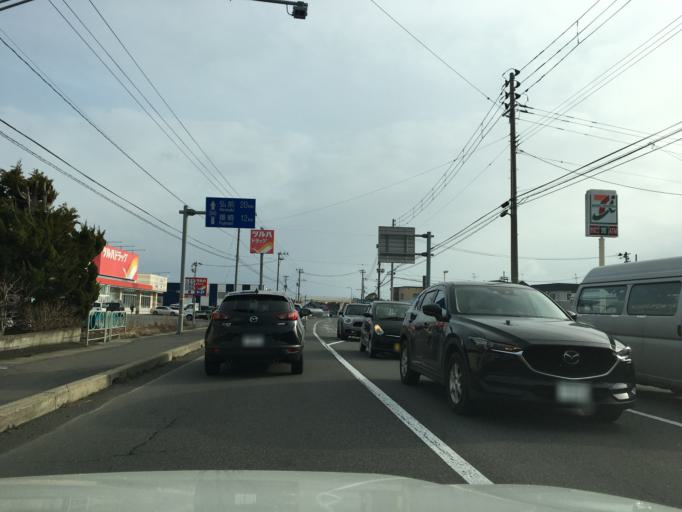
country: JP
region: Aomori
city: Namioka
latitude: 40.7214
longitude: 140.5889
